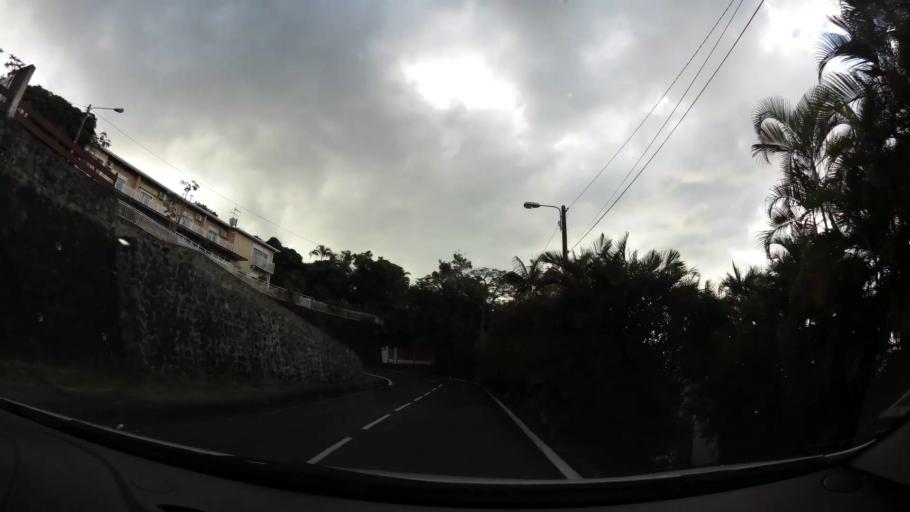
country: RE
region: Reunion
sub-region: Reunion
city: Saint-Denis
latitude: -20.9021
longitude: 55.4436
